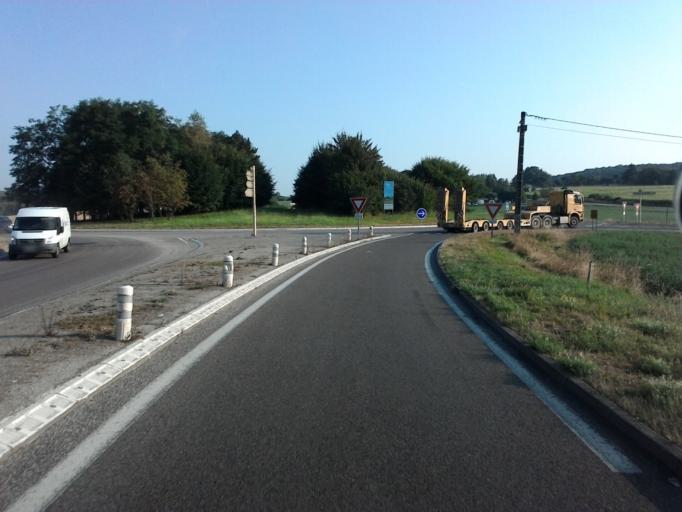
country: FR
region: Franche-Comte
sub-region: Departement de la Haute-Saone
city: Echenoz-la-Meline
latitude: 47.5739
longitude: 6.1388
